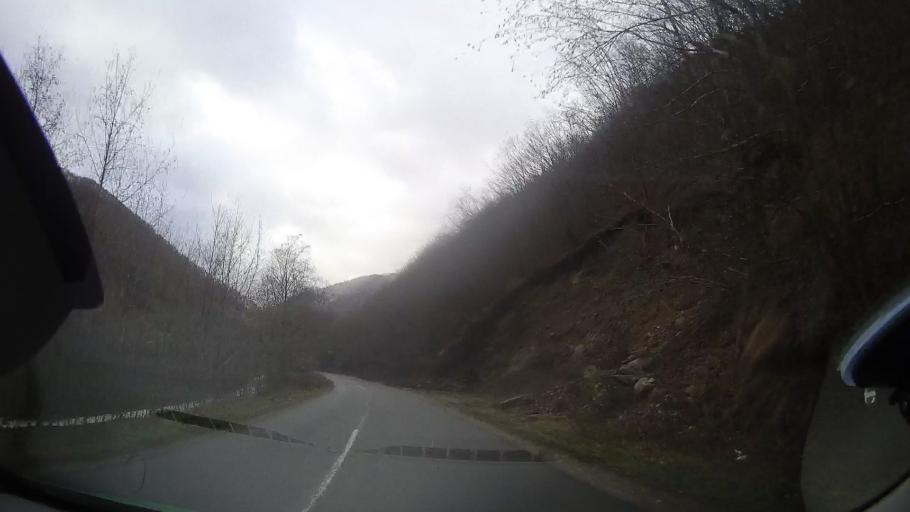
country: RO
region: Cluj
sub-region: Comuna Maguri-Racatau
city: Maguri-Racatau
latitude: 46.6560
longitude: 23.2111
